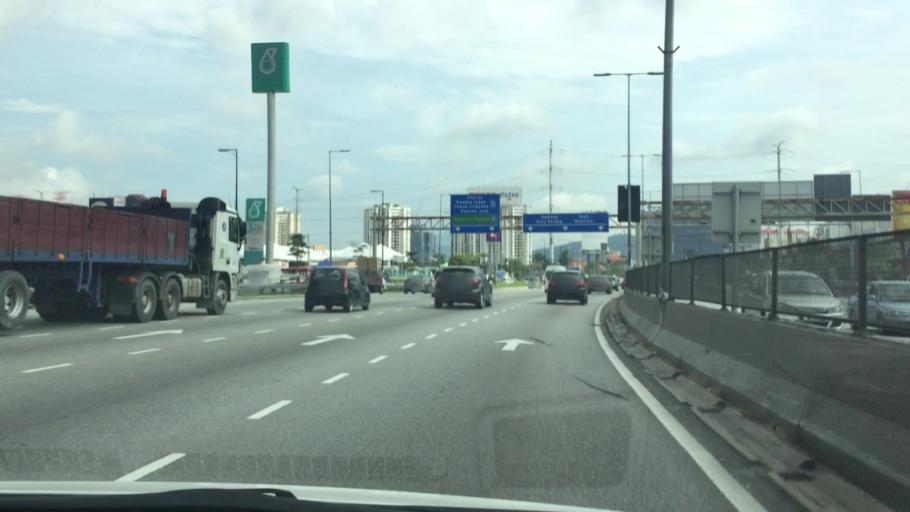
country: MY
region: Kuala Lumpur
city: Kuala Lumpur
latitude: 3.1407
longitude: 101.7430
